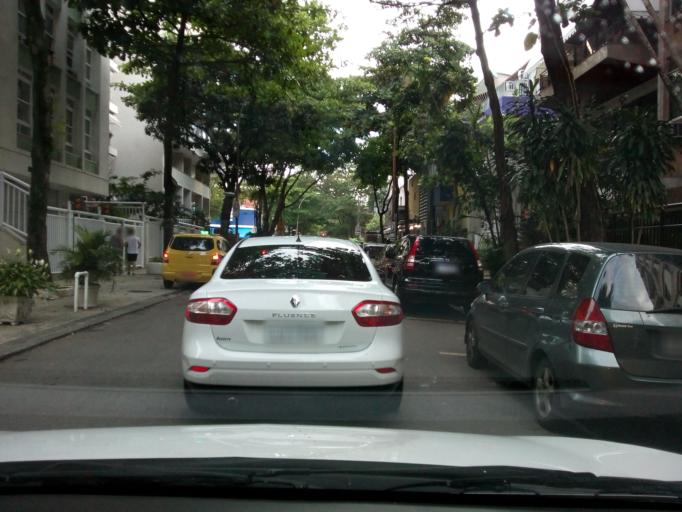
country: BR
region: Rio de Janeiro
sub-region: Rio De Janeiro
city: Rio de Janeiro
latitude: -22.9815
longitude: -43.2006
